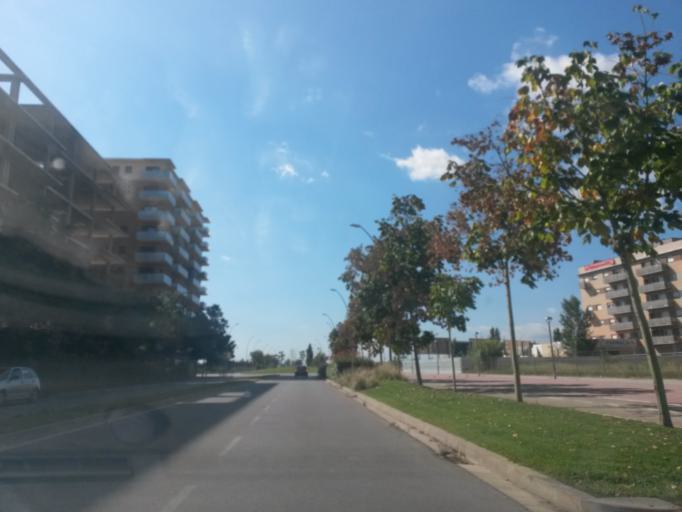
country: ES
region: Catalonia
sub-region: Provincia de Girona
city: Salt
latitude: 41.9719
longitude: 2.8005
